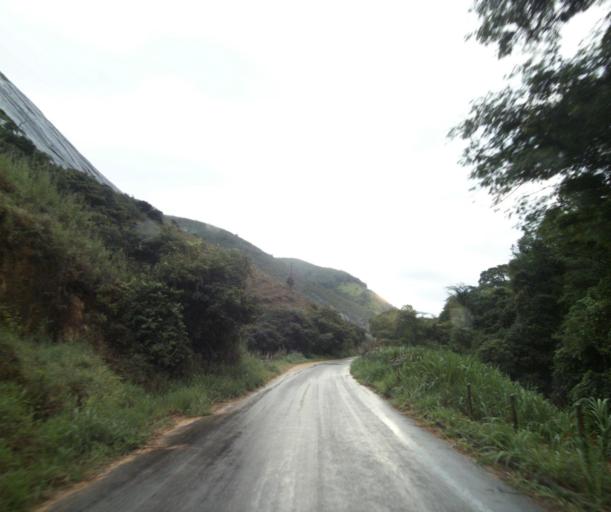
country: BR
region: Espirito Santo
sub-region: Muniz Freire
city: Muniz Freire
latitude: -20.4625
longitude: -41.4250
